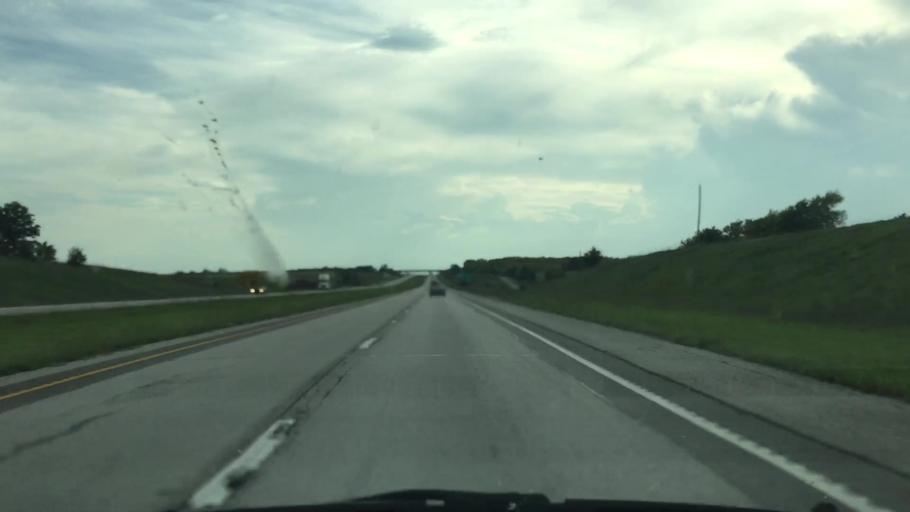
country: US
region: Missouri
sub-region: Harrison County
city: Bethany
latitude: 40.1466
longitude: -94.0393
